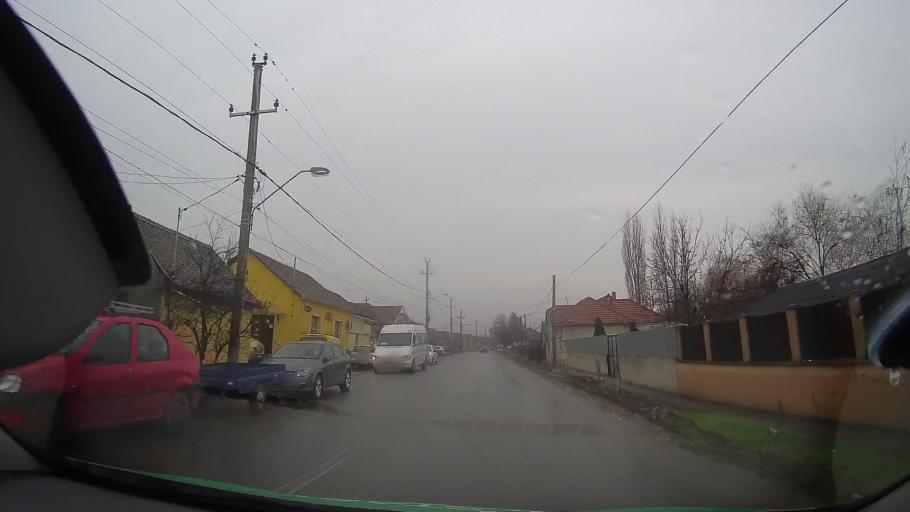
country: RO
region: Bihor
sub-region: Municipiul Salonta
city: Salonta
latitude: 46.7969
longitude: 21.6569
